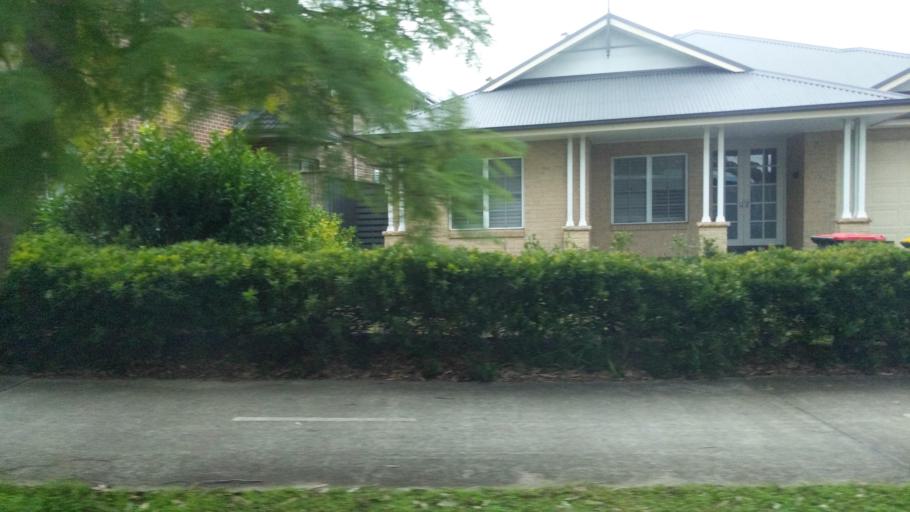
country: AU
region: New South Wales
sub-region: Blacktown
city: Quakers Hill
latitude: -33.7268
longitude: 150.8632
